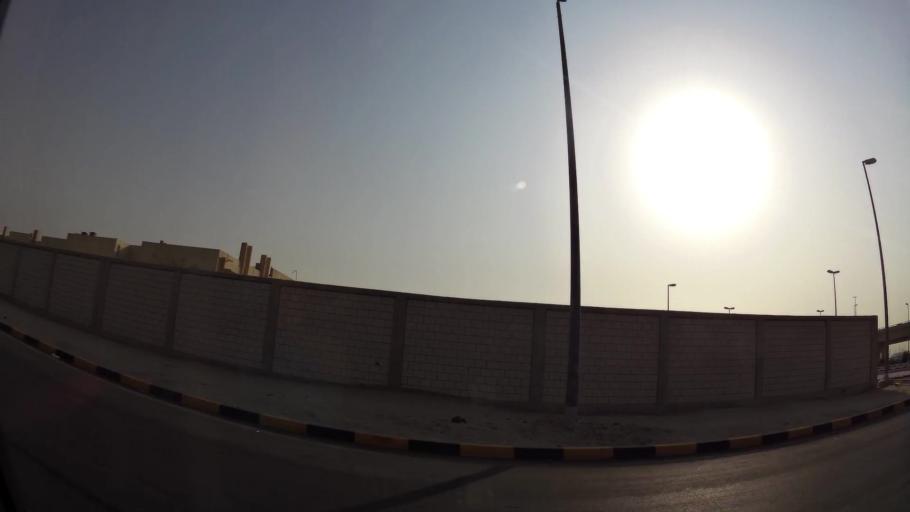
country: KW
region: Al Asimah
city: Ar Rabiyah
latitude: 29.3128
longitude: 47.8063
